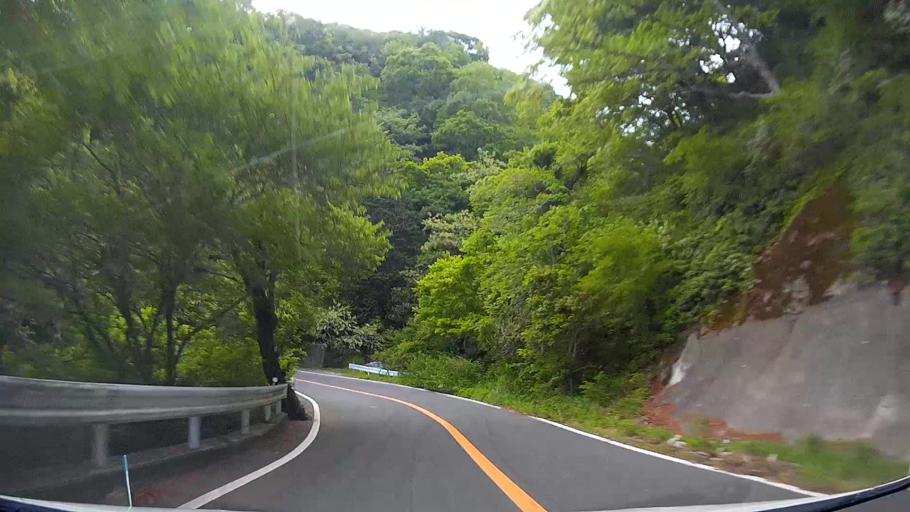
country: JP
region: Kanagawa
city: Yugawara
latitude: 35.1578
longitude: 139.0690
